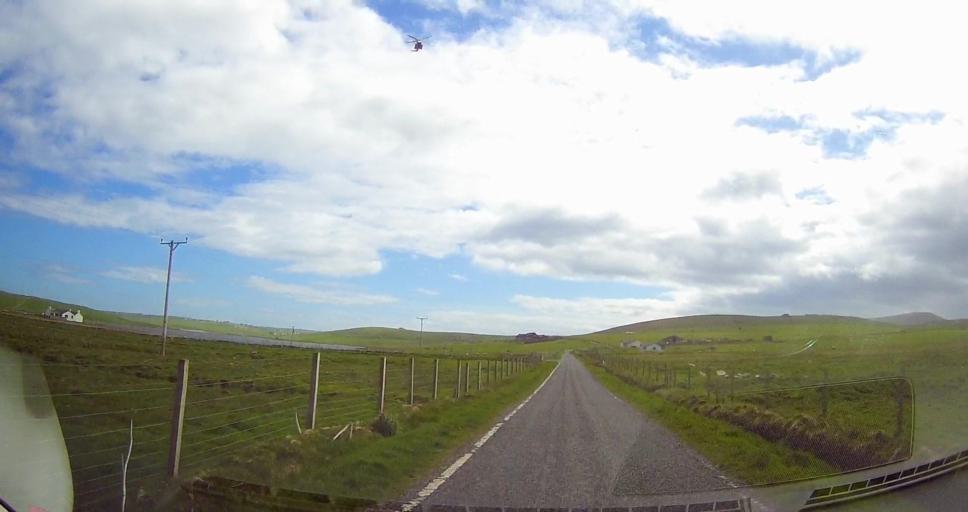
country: GB
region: Scotland
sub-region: Shetland Islands
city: Sandwick
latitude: 59.9370
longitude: -1.3460
